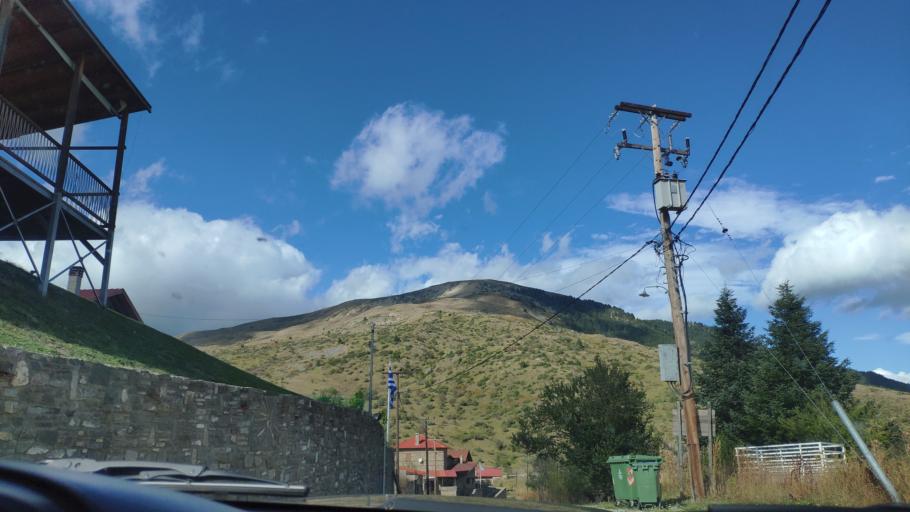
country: AL
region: Korce
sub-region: Rrethi i Devollit
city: Miras
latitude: 40.3931
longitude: 20.8367
